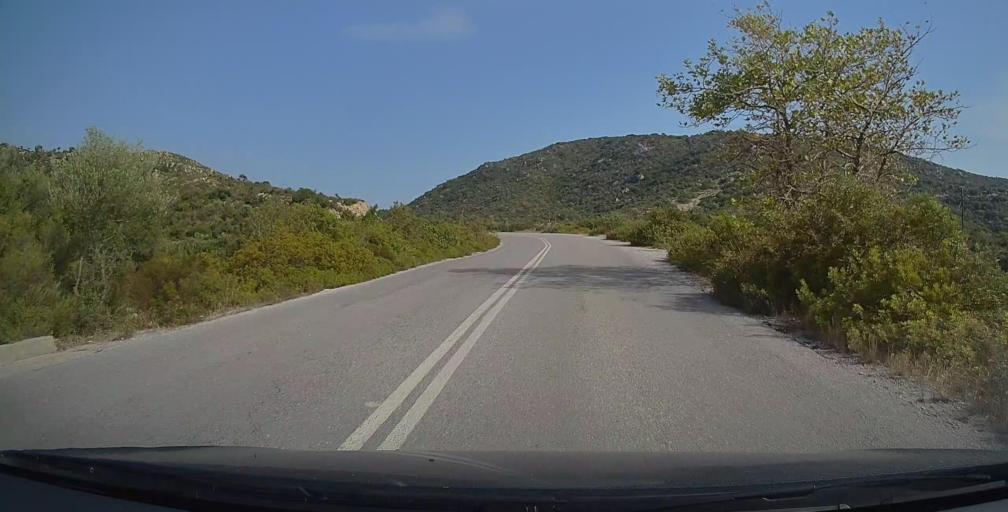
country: GR
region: Central Macedonia
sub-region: Nomos Chalkidikis
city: Sykia
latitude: 39.9950
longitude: 23.9864
